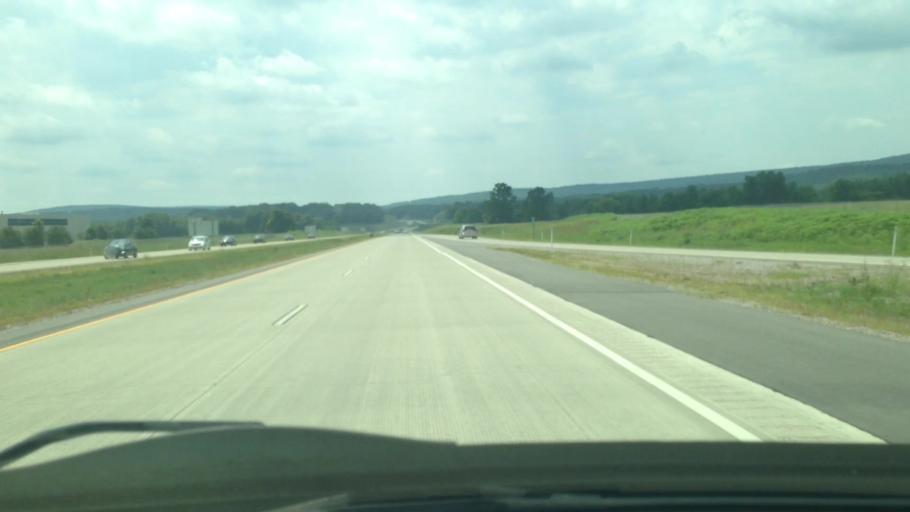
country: US
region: Wisconsin
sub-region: Sauk County
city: West Baraboo
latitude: 43.4571
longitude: -89.7783
